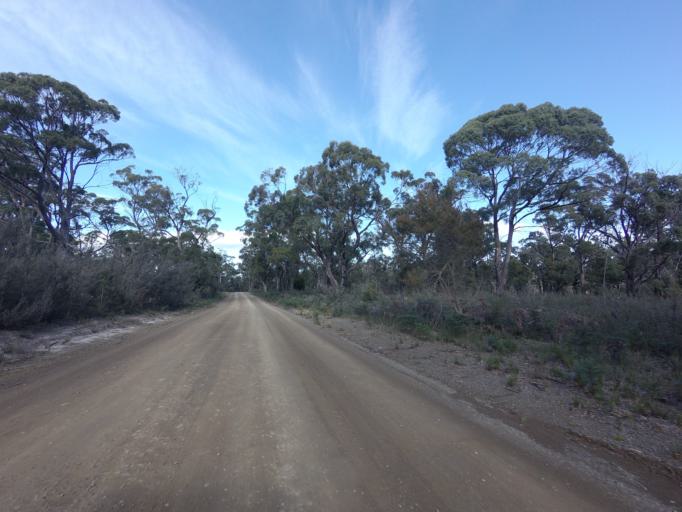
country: AU
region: Tasmania
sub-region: Clarence
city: Sandford
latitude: -42.9836
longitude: 147.7122
